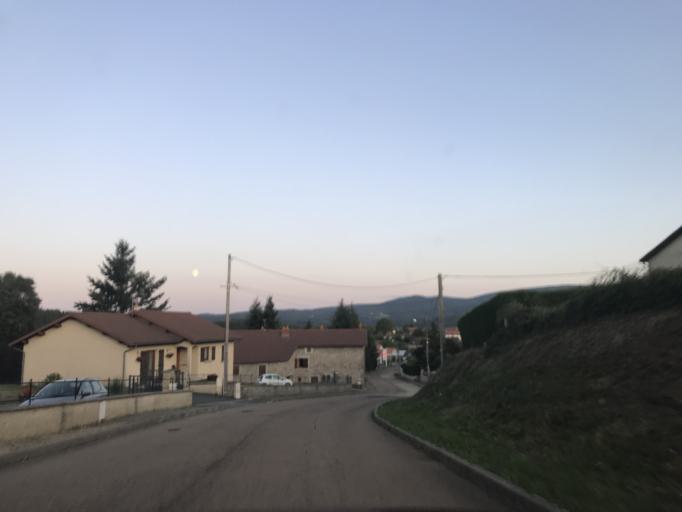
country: FR
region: Rhone-Alpes
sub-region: Departement de la Loire
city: Noiretable
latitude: 45.8235
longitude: 3.7634
